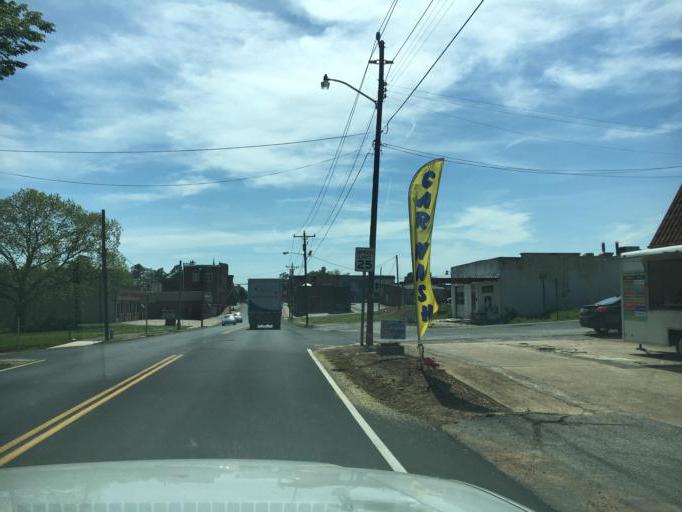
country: US
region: South Carolina
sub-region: Cherokee County
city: Blacksburg
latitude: 35.1220
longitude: -81.5141
